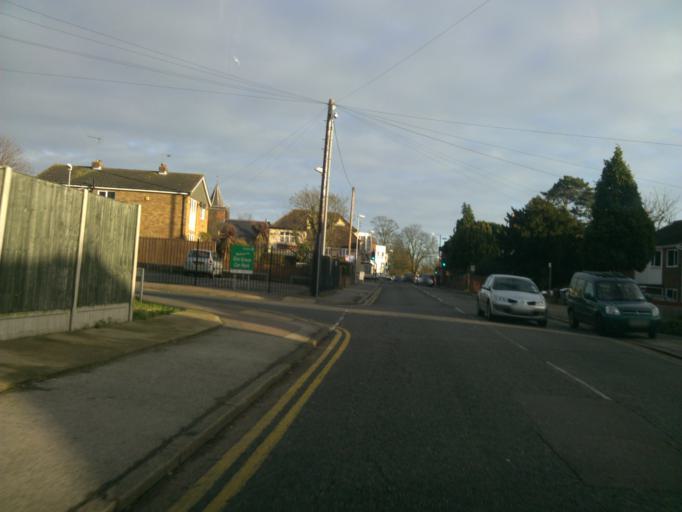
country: GB
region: England
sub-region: Essex
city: Clacton-on-Sea
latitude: 51.8049
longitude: 1.1532
